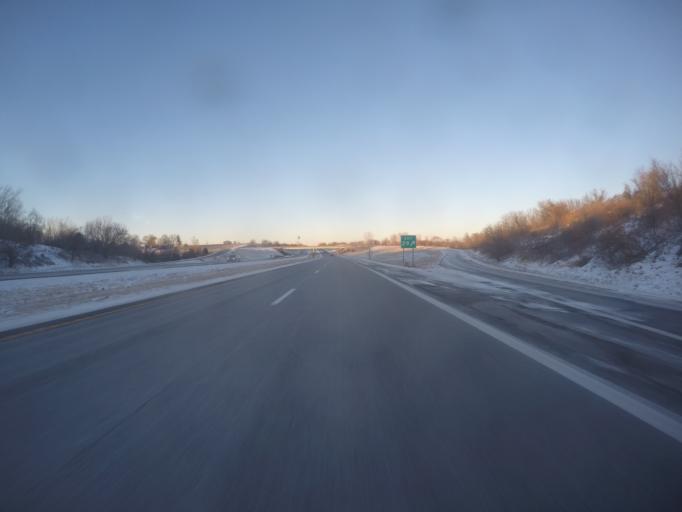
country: US
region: Missouri
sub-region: Platte County
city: Platte City
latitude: 39.3078
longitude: -94.7588
